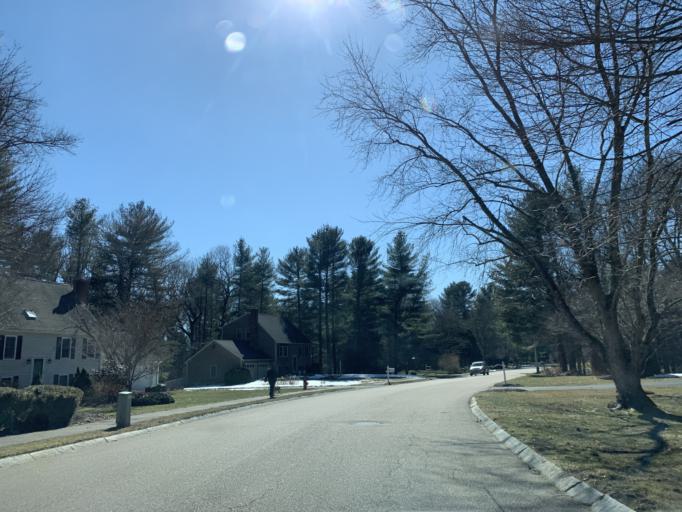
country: US
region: Massachusetts
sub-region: Bristol County
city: Norton
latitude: 41.9482
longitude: -71.1941
